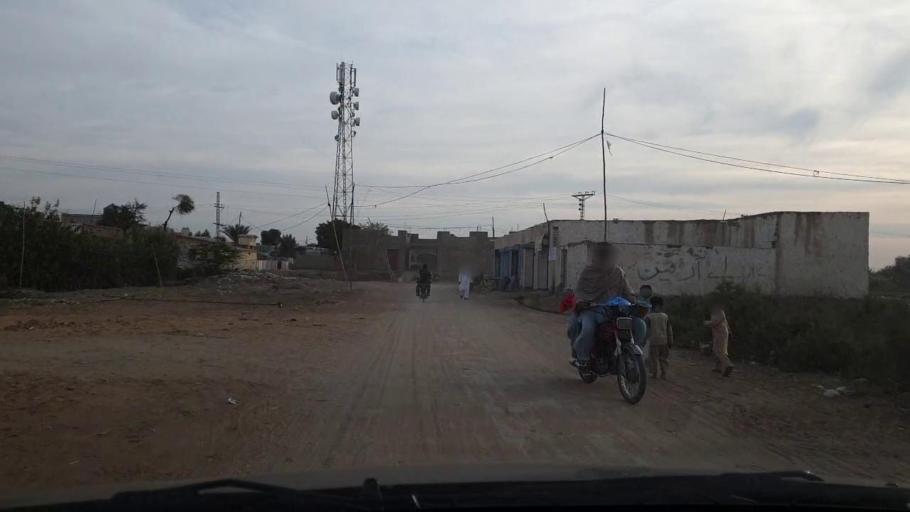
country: PK
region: Sindh
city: Khadro
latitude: 26.1499
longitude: 68.7148
